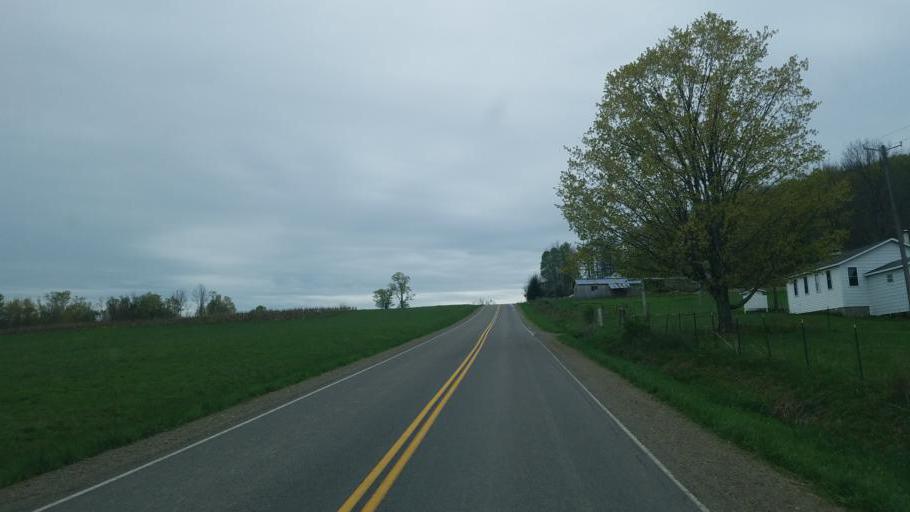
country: US
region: Pennsylvania
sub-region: Tioga County
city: Westfield
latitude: 42.0396
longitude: -77.4663
